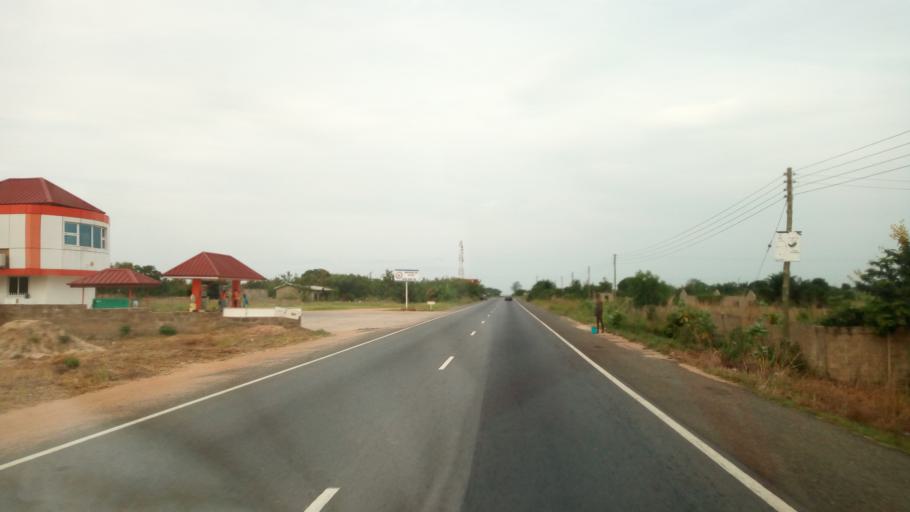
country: GH
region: Volta
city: Keta
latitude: 6.0649
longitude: 1.0095
